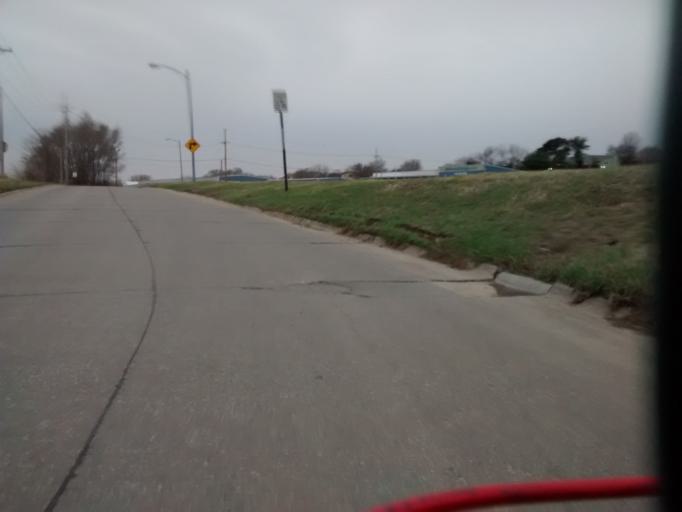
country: US
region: Nebraska
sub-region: Sarpy County
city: Offutt Air Force Base
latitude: 41.1648
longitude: -95.9261
